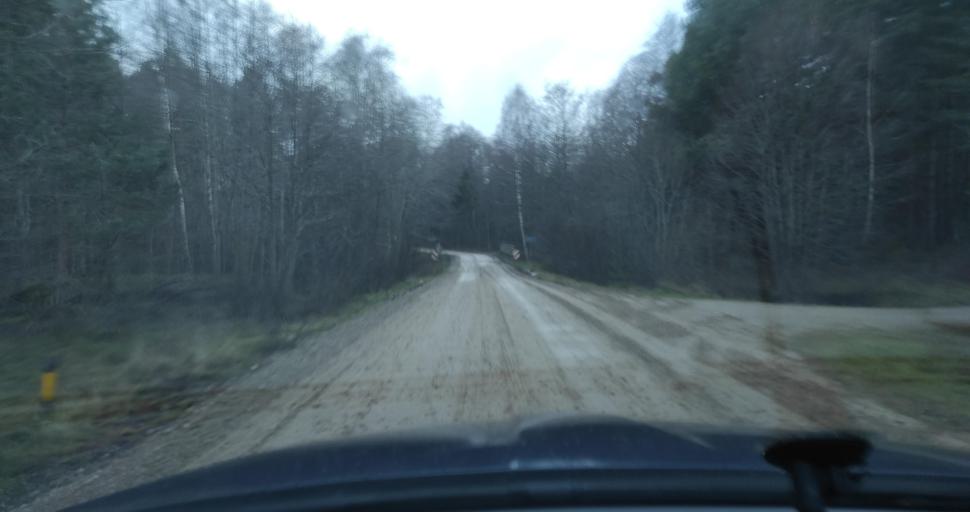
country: LV
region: Pavilostas
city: Pavilosta
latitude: 56.8424
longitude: 21.0865
